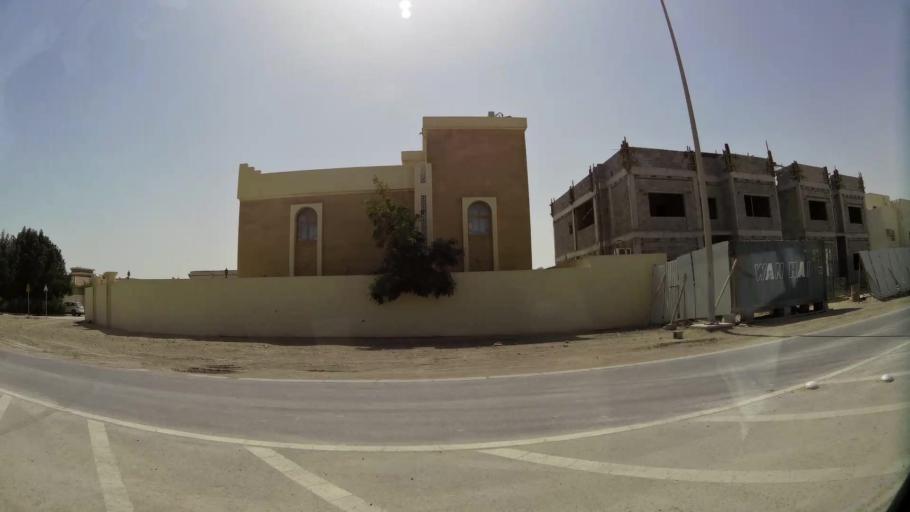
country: QA
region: Baladiyat Umm Salal
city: Umm Salal Muhammad
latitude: 25.3706
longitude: 51.4421
